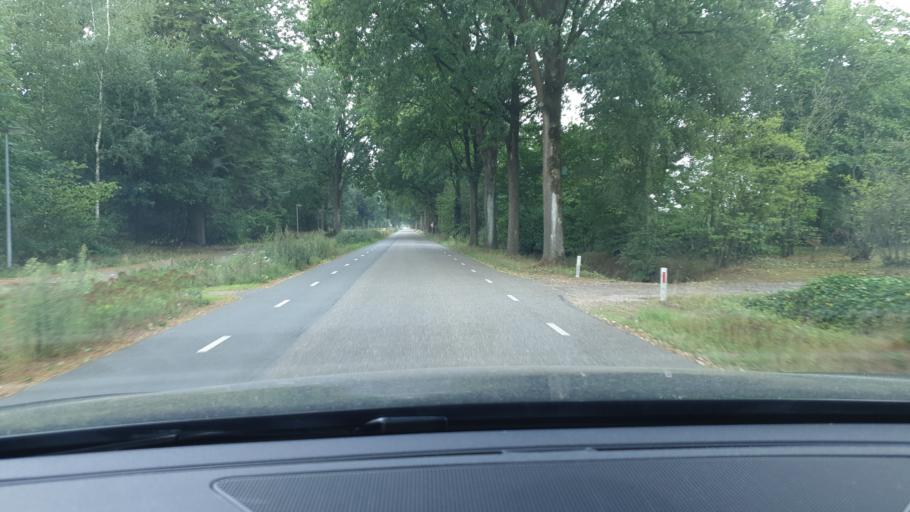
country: NL
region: North Brabant
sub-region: Gemeente Veldhoven
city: Oerle
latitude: 51.4431
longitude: 5.3200
